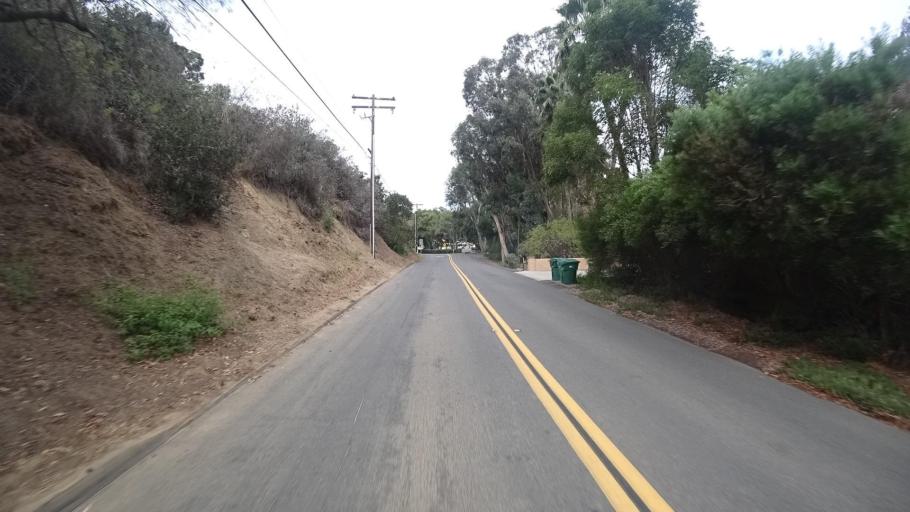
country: US
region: California
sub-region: San Diego County
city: Rancho Santa Fe
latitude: 32.9899
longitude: -117.2279
